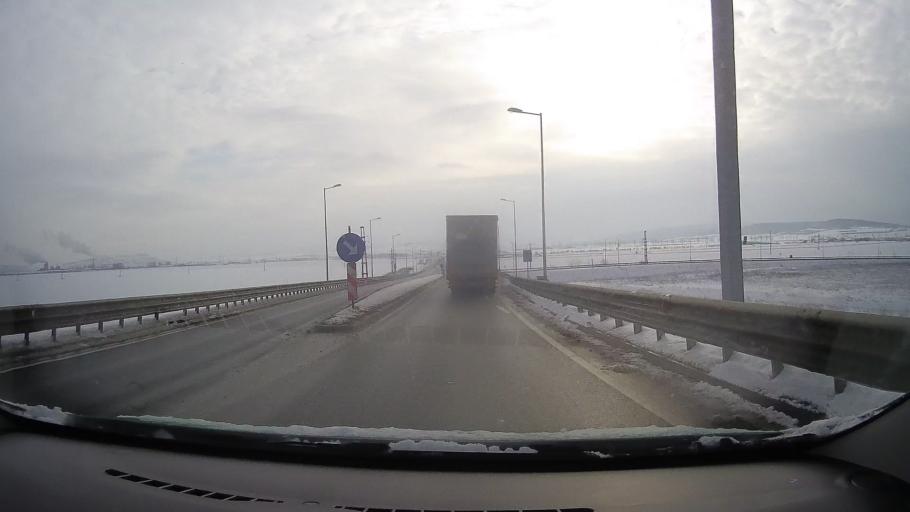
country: RO
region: Alba
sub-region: Municipiul Sebes
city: Lancram
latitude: 45.9765
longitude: 23.5221
